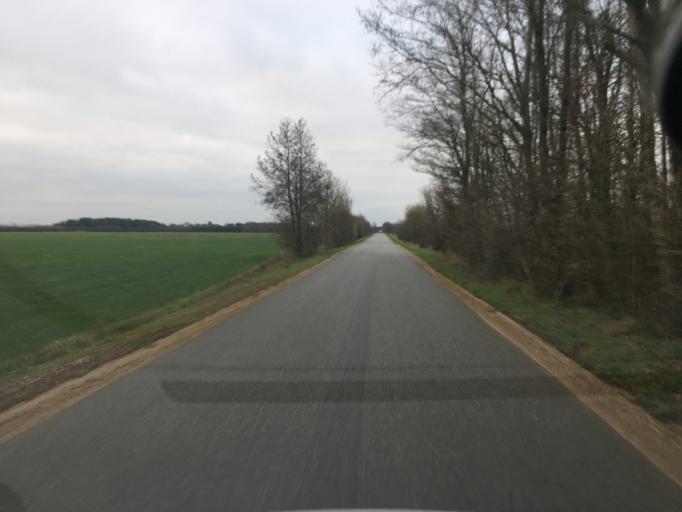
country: DK
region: South Denmark
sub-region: Tonder Kommune
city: Logumkloster
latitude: 55.0351
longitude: 9.0294
